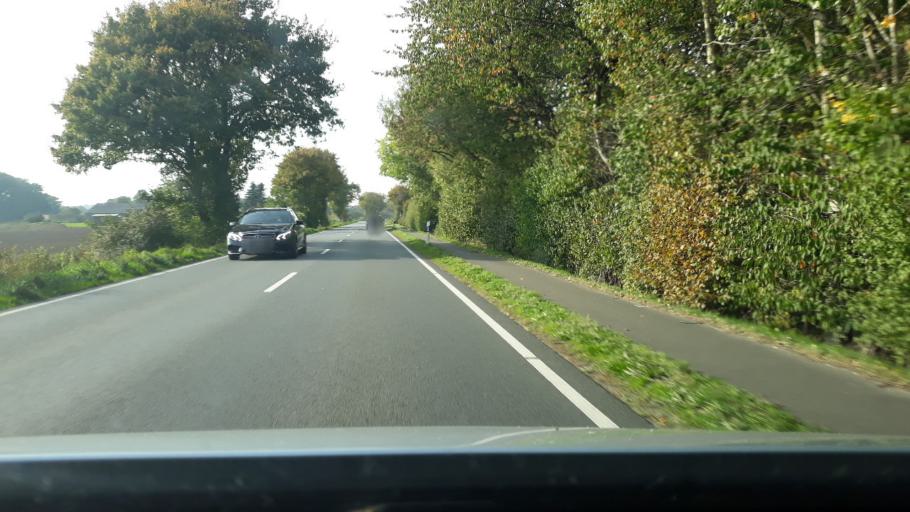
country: DE
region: Schleswig-Holstein
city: Brekendorf
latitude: 54.4011
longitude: 9.6297
